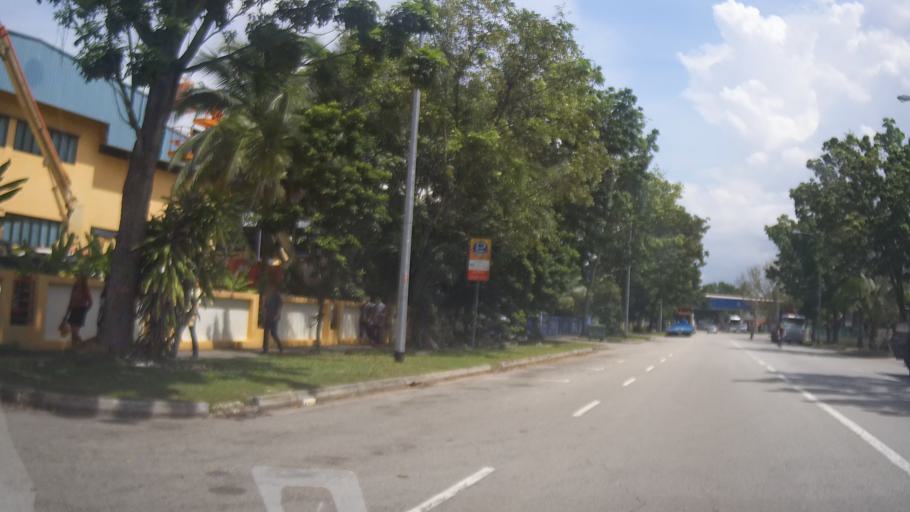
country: MY
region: Johor
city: Johor Bahru
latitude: 1.4064
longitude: 103.7514
